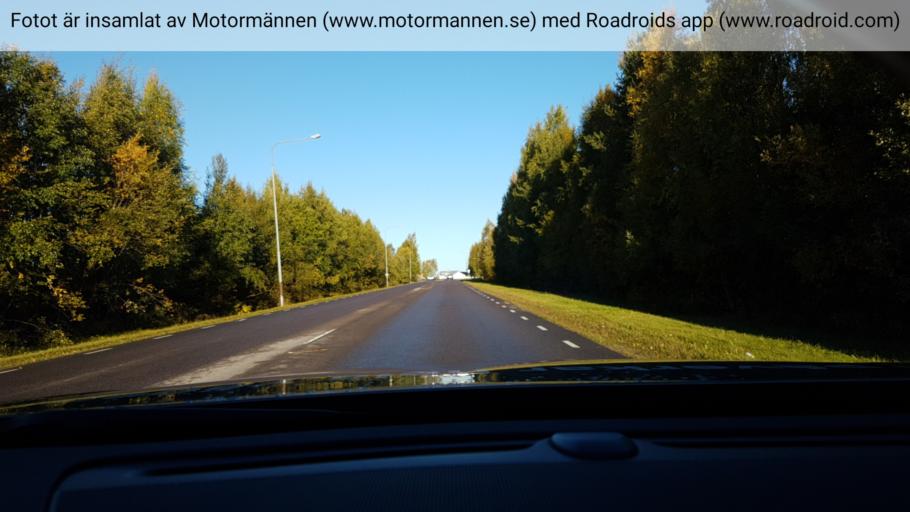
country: SE
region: Norrbotten
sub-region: Lulea Kommun
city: Sodra Sunderbyn
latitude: 65.6605
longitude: 21.9501
